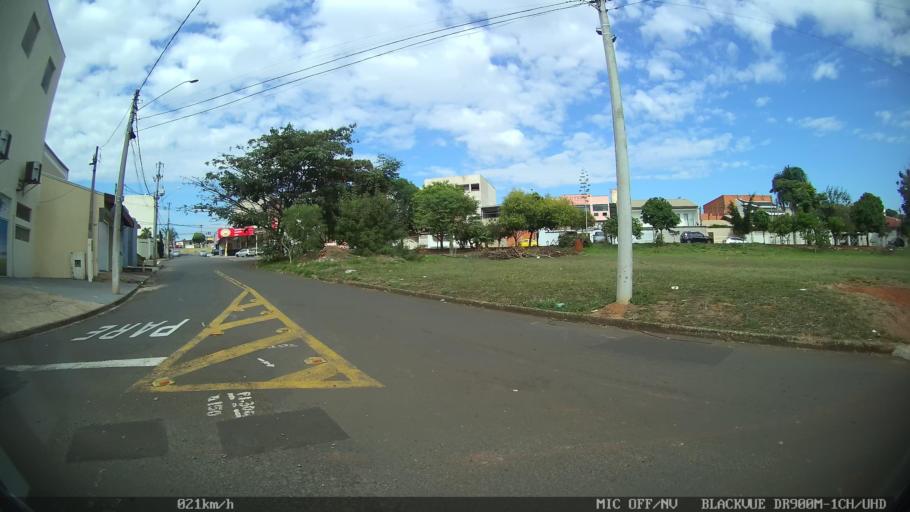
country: BR
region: Sao Paulo
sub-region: Americana
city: Americana
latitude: -22.7369
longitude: -47.3702
